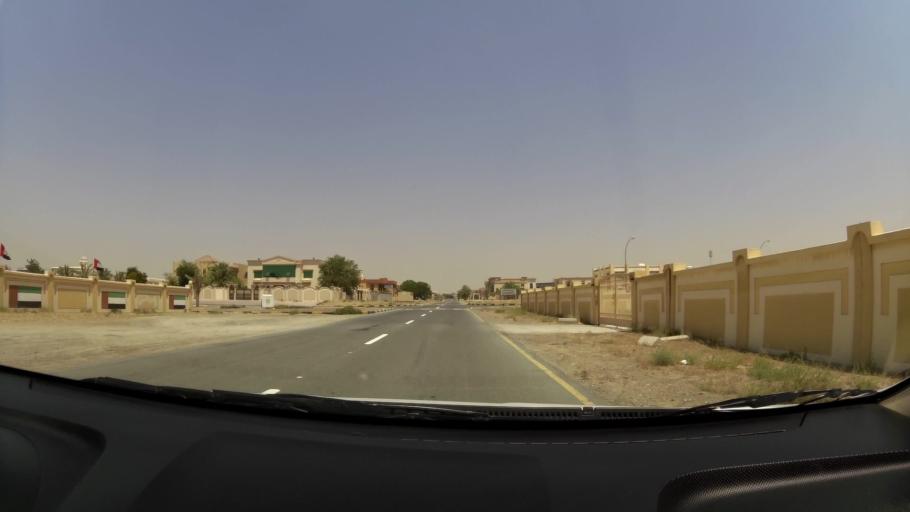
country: AE
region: Ajman
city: Ajman
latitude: 25.4259
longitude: 55.5112
